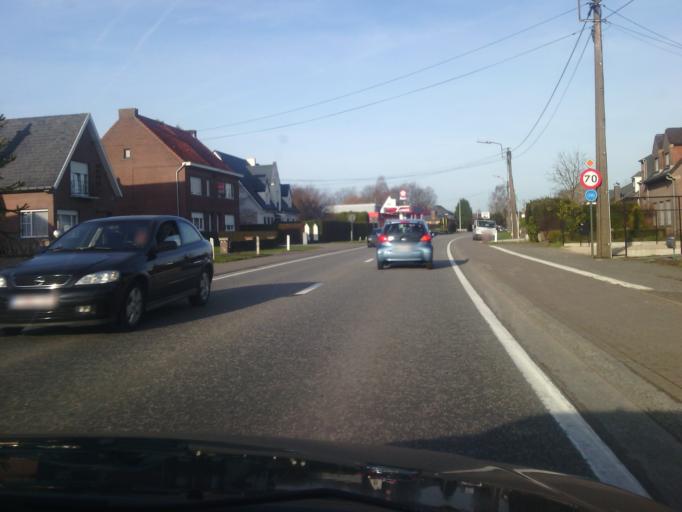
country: BE
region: Flanders
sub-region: Provincie Oost-Vlaanderen
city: Lede
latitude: 50.9568
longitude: 3.9777
